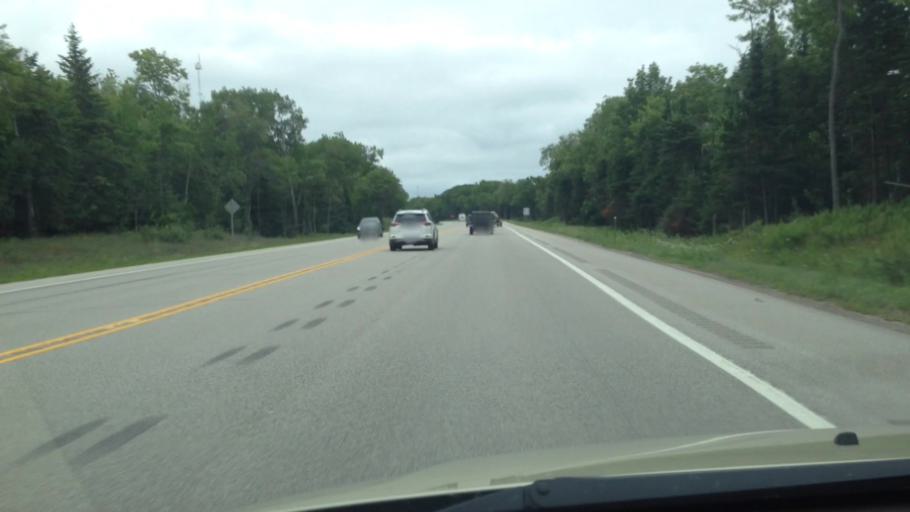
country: US
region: Michigan
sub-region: Luce County
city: Newberry
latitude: 46.0682
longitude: -85.1953
